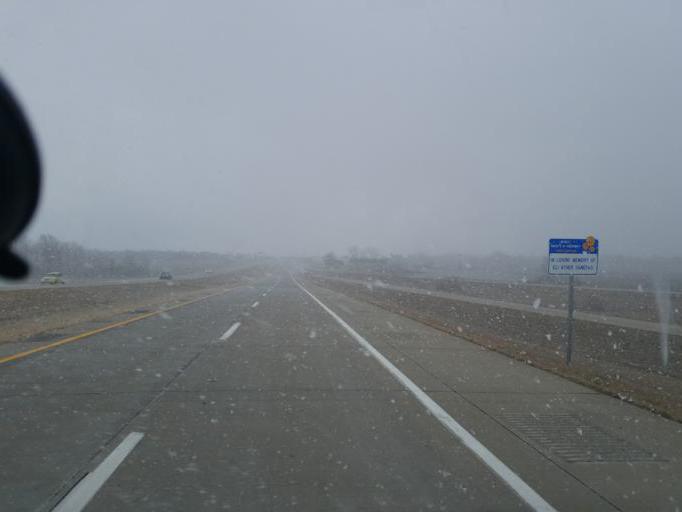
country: US
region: Missouri
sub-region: Randolph County
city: Moberly
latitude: 39.4425
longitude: -92.4236
